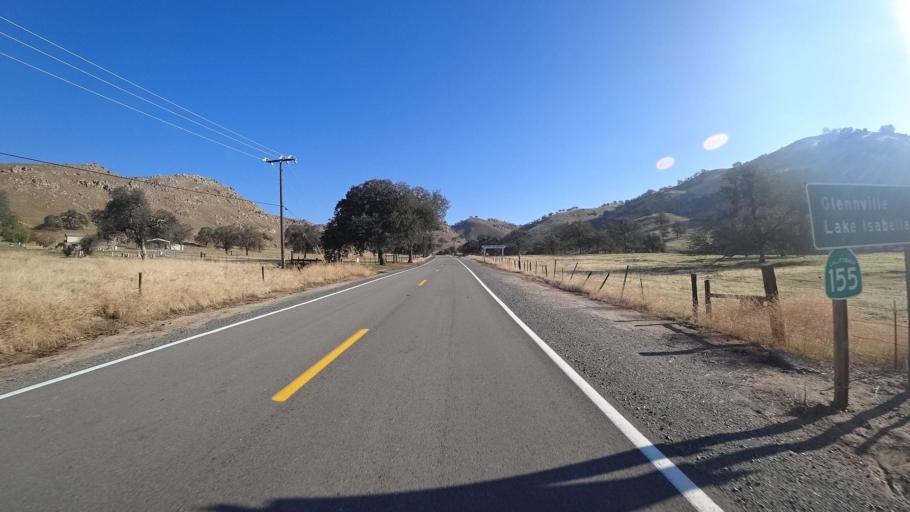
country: US
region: California
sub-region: Kern County
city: Alta Sierra
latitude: 35.7058
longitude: -118.8312
